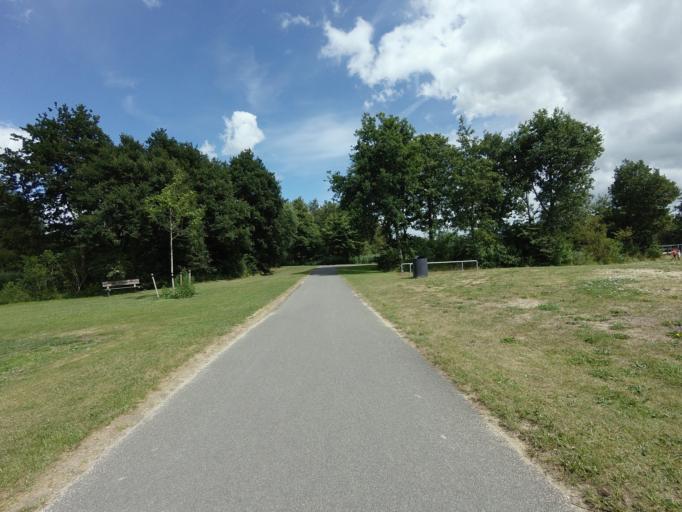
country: NL
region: North Holland
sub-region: Gemeente Zaanstad
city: Zaanstad
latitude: 52.4644
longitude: 4.8397
